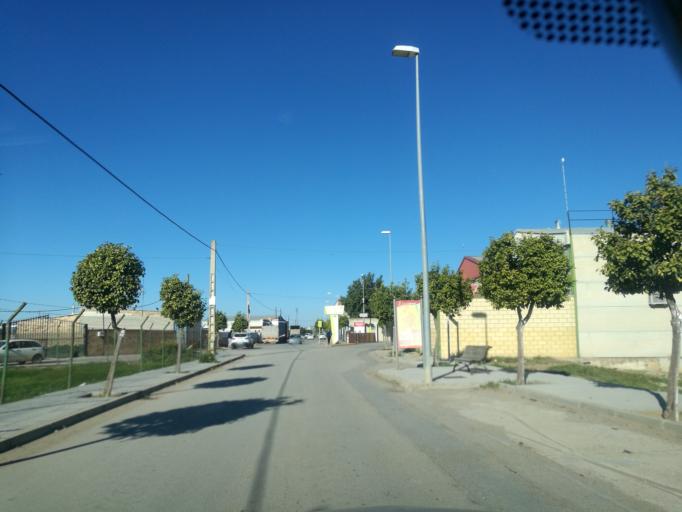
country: ES
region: Andalusia
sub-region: Provincia de Sevilla
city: La Campana
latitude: 37.5736
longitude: -5.4300
